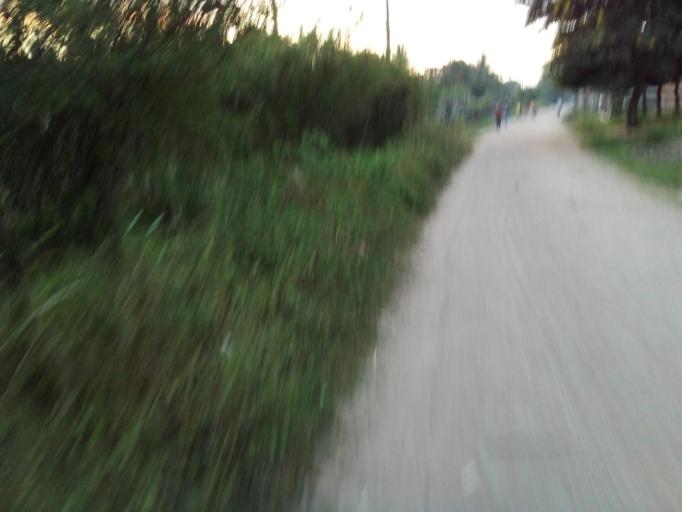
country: MZ
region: Zambezia
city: Quelimane
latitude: -17.6040
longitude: 36.8151
